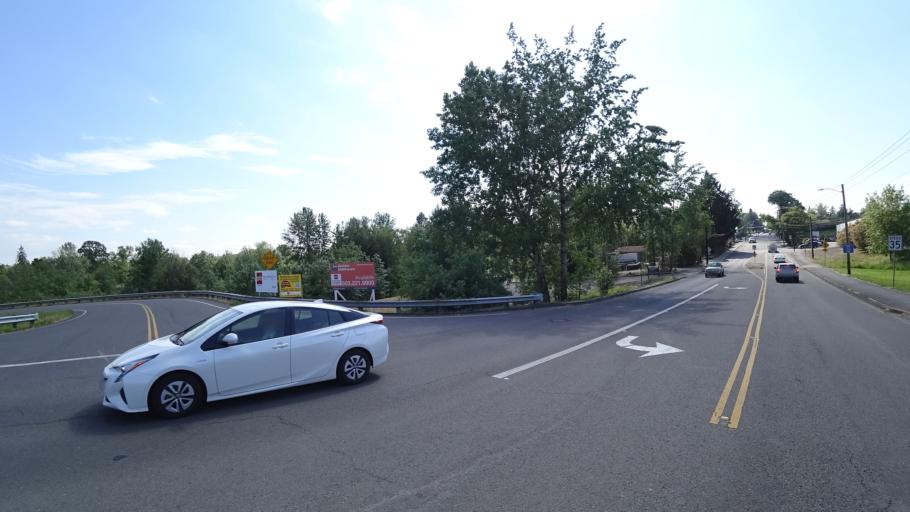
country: US
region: Oregon
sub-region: Washington County
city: Beaverton
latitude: 45.4694
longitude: -122.7895
